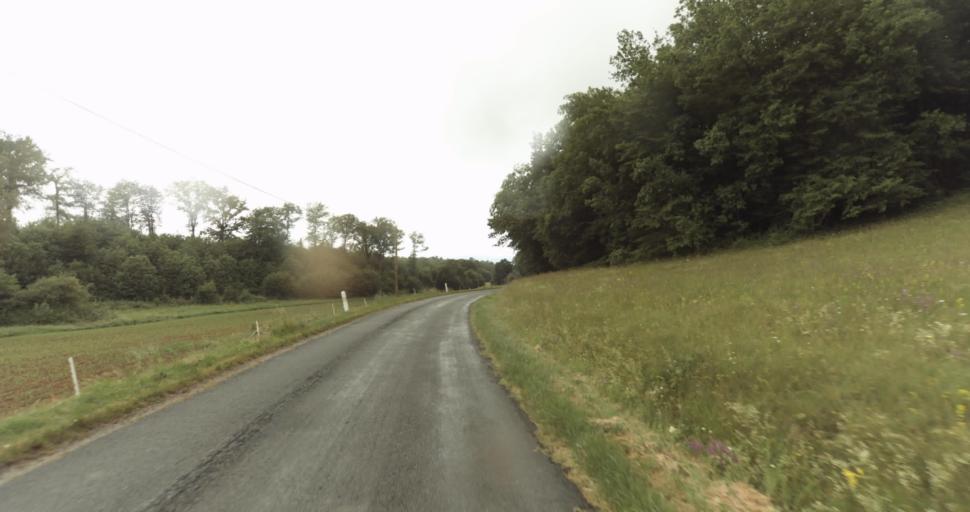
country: FR
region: Aquitaine
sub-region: Departement de la Dordogne
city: Belves
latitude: 44.7542
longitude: 0.9337
